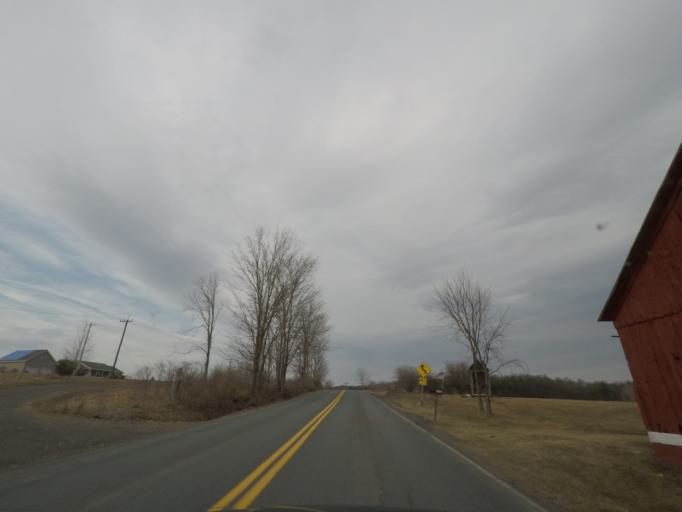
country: US
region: New York
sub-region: Washington County
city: Cambridge
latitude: 42.9385
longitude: -73.4919
